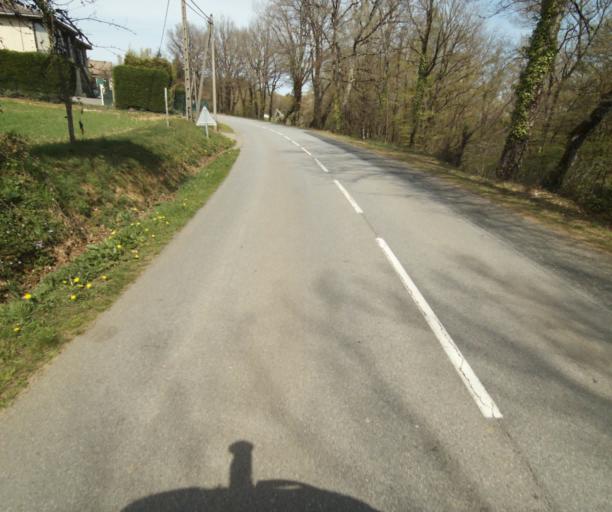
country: FR
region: Limousin
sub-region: Departement de la Correze
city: Naves
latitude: 45.3754
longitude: 1.8032
